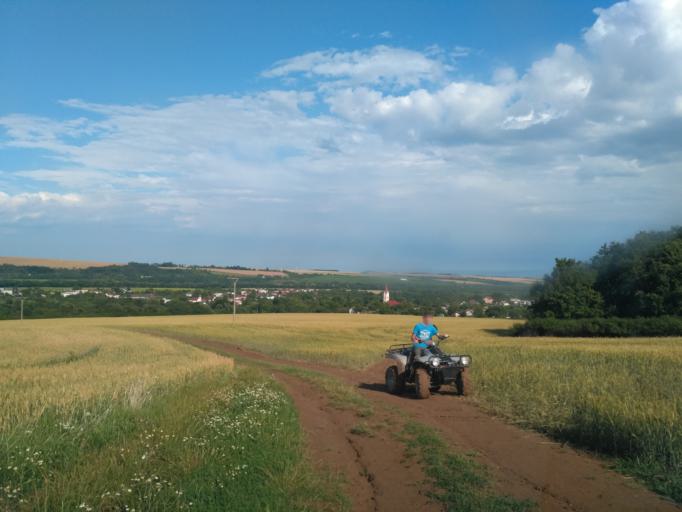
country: SK
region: Kosicky
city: Secovce
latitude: 48.6016
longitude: 21.5437
